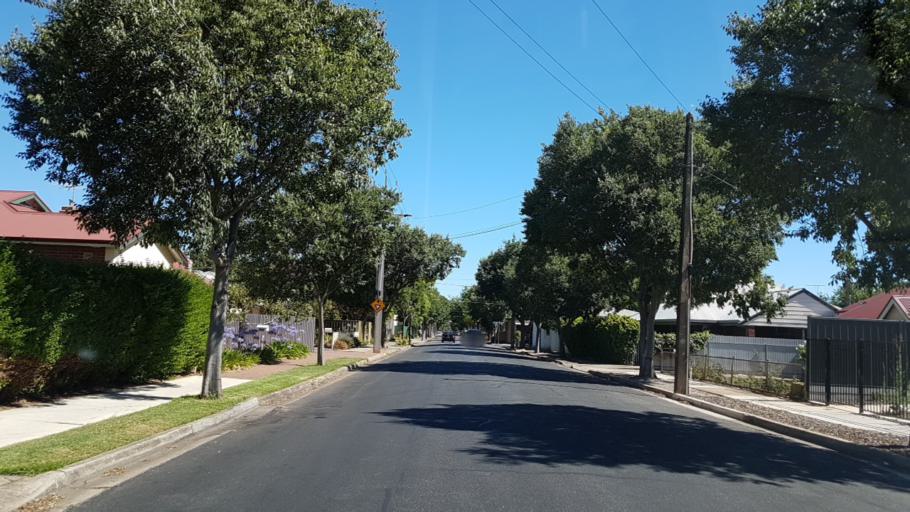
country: AU
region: South Australia
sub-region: City of West Torrens
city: Thebarton
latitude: -34.9157
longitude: 138.5606
